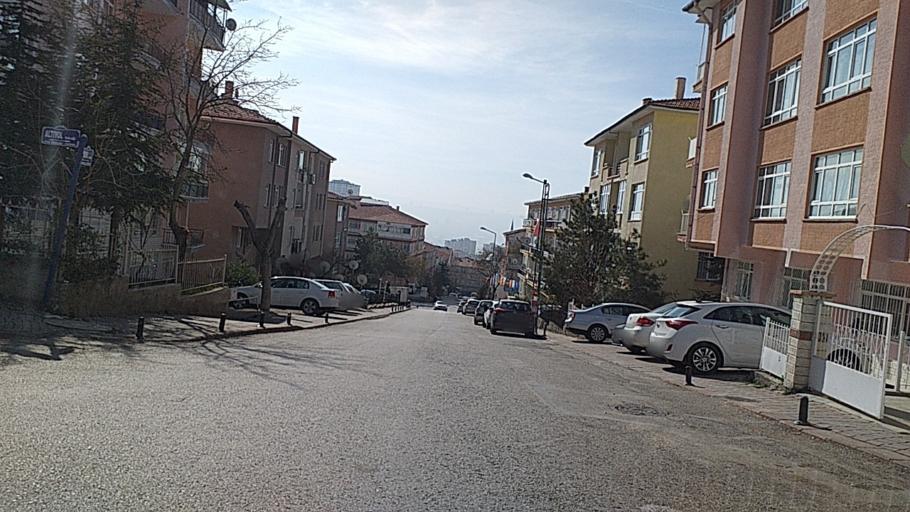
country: TR
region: Ankara
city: Ankara
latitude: 39.9810
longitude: 32.8300
